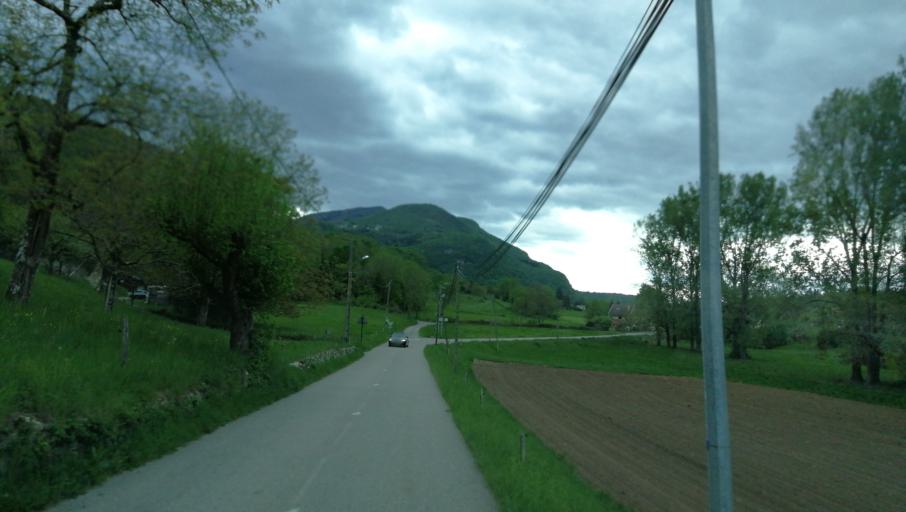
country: FR
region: Rhone-Alpes
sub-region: Departement de la Savoie
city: Chatillon
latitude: 45.7827
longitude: 5.8178
